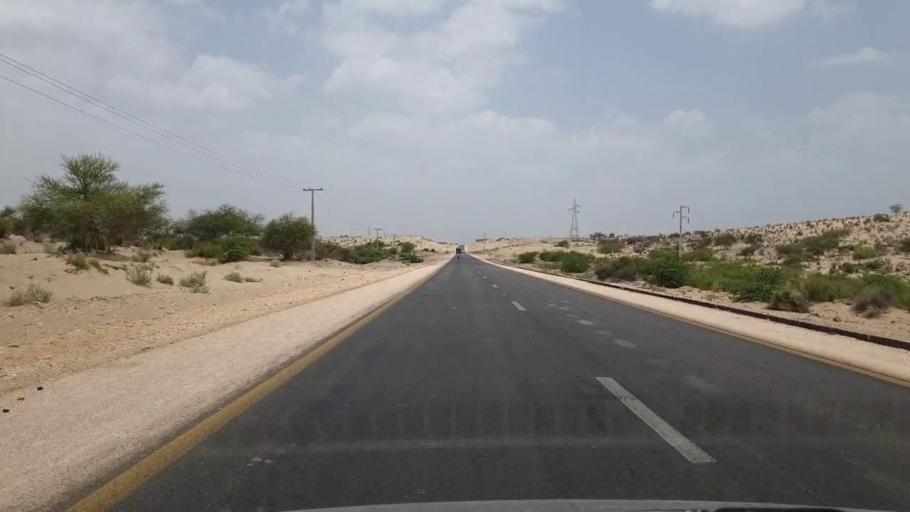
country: PK
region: Sindh
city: Naukot
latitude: 24.8368
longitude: 69.4671
